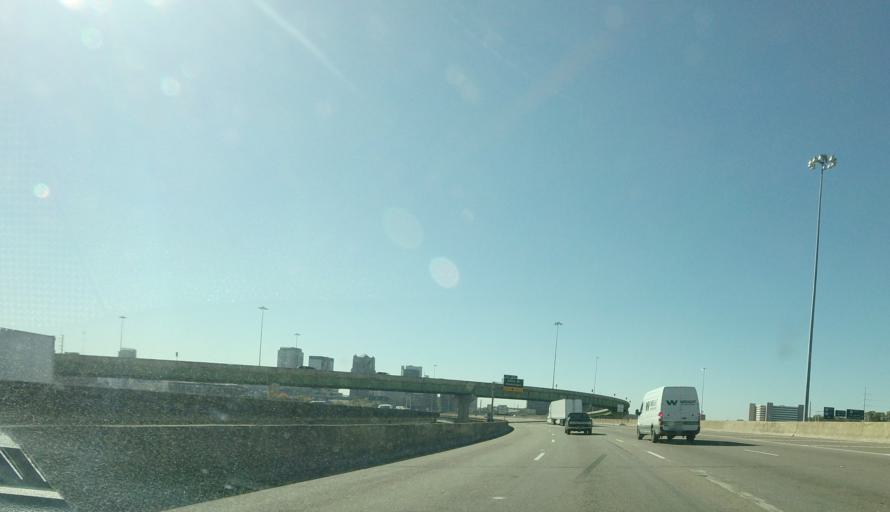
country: US
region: Alabama
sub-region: Jefferson County
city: Birmingham
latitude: 33.5295
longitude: -86.8034
